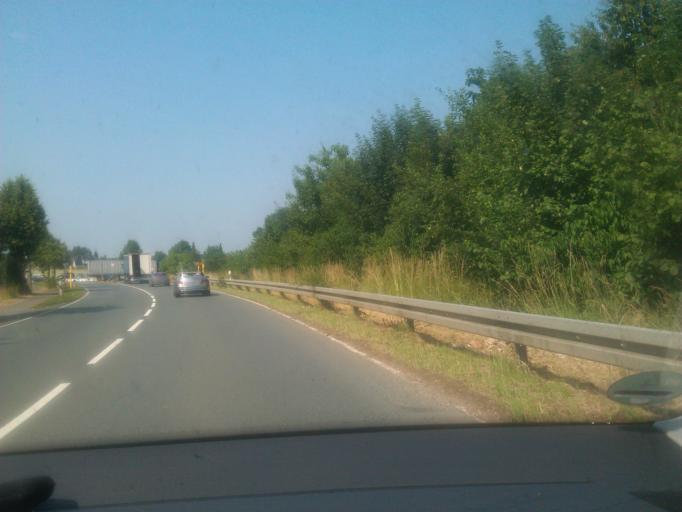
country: DE
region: North Rhine-Westphalia
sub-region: Regierungsbezirk Detmold
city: Bad Salzuflen
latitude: 52.0509
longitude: 8.7400
